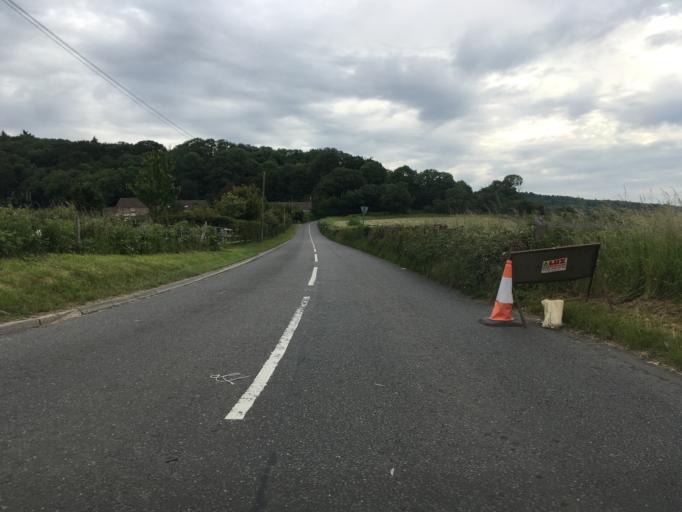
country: GB
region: England
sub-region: North Somerset
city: Long Ashton
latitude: 51.4269
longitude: -2.7012
